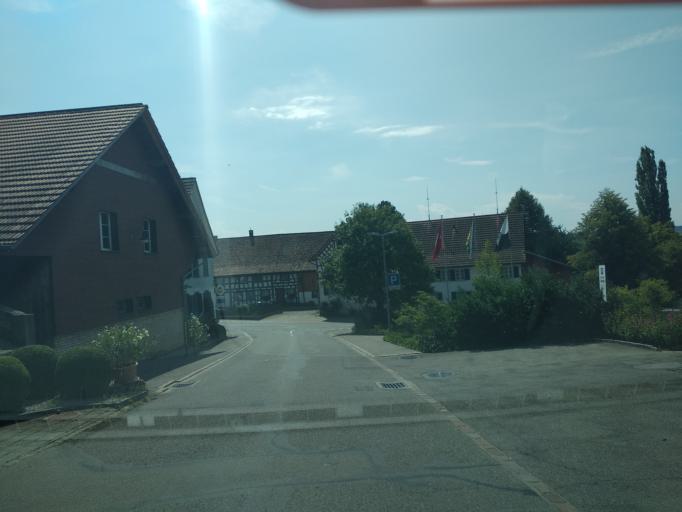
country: CH
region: Thurgau
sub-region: Frauenfeld District
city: Gachnang
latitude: 47.5807
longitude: 8.8311
